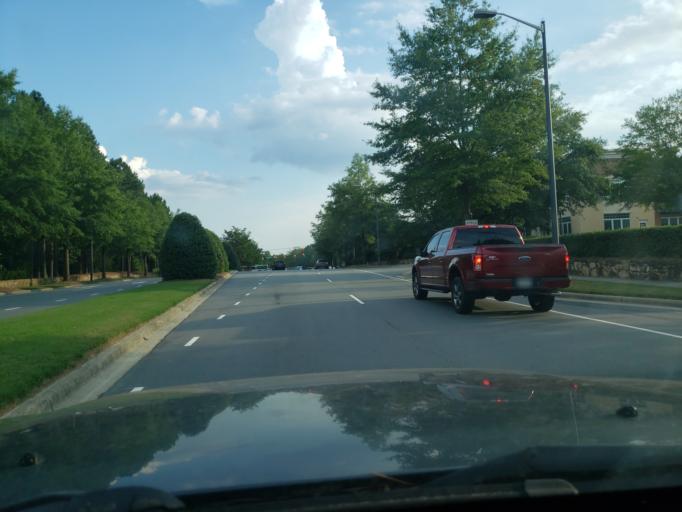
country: US
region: North Carolina
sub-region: Orange County
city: Chapel Hill
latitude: 35.9042
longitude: -79.0097
